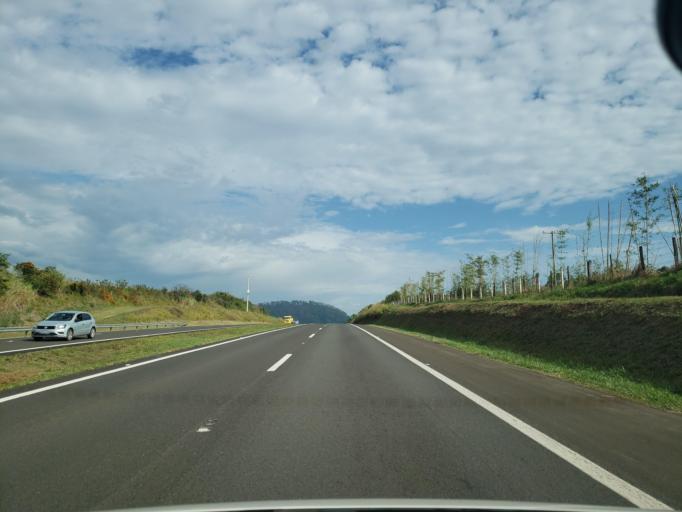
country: BR
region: Sao Paulo
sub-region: Dois Corregos
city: Dois Corregos
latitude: -22.2437
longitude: -48.3169
